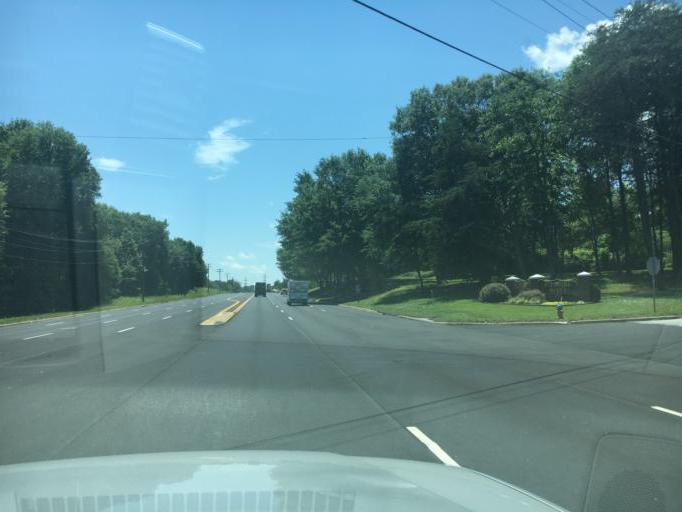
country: US
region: South Carolina
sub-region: Greenville County
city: Berea
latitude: 34.9219
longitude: -82.4583
